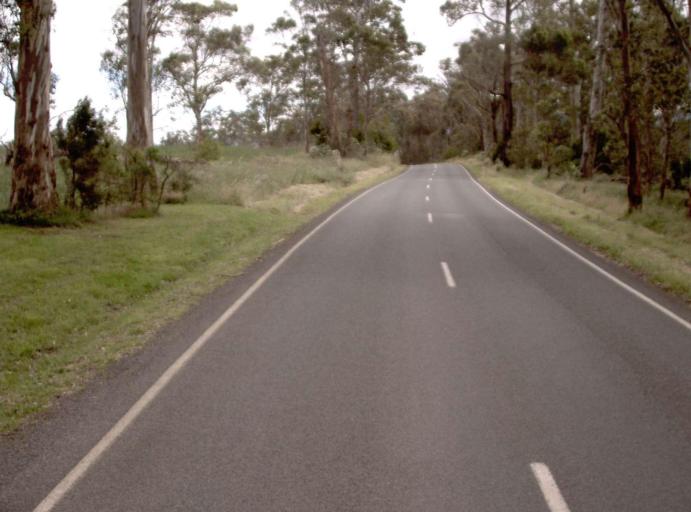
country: AU
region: Victoria
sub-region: Latrobe
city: Moe
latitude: -38.0416
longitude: 146.1671
